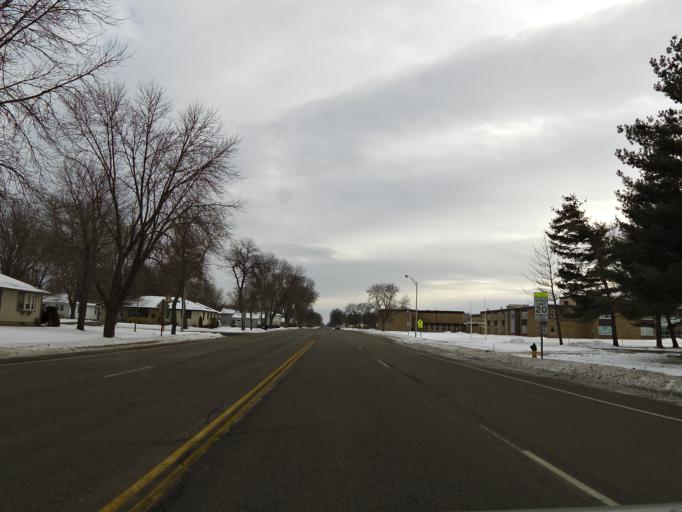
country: US
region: Minnesota
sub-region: Scott County
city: Shakopee
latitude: 44.7883
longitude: -93.5255
